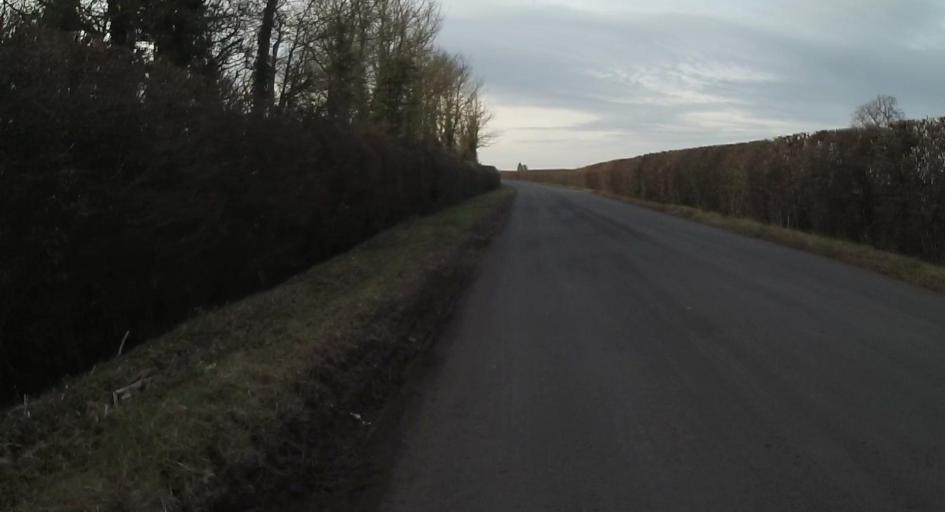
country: GB
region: England
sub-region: West Berkshire
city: Stratfield Mortimer
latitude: 51.4044
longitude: -1.0336
